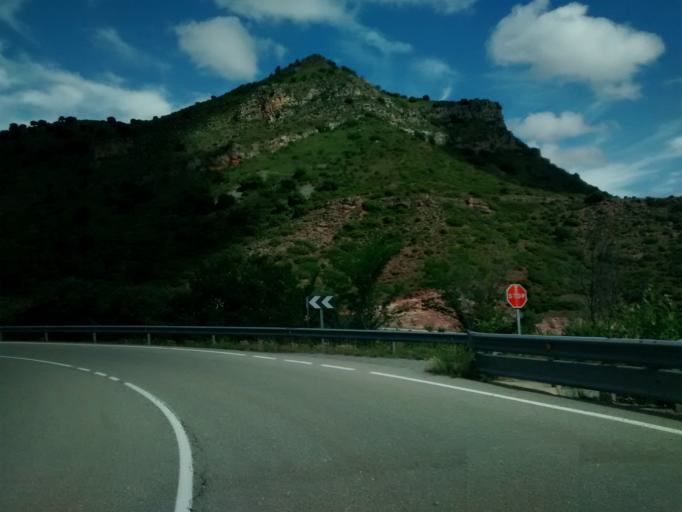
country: ES
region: La Rioja
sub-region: Provincia de La Rioja
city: Leza de Rio Leza
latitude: 42.3205
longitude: -2.4150
